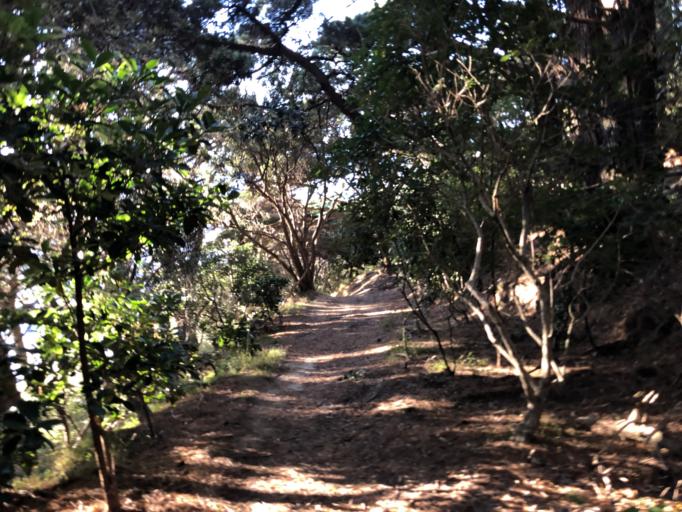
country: NZ
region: Wellington
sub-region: Wellington City
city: Wellington
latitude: -41.2999
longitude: 174.7887
